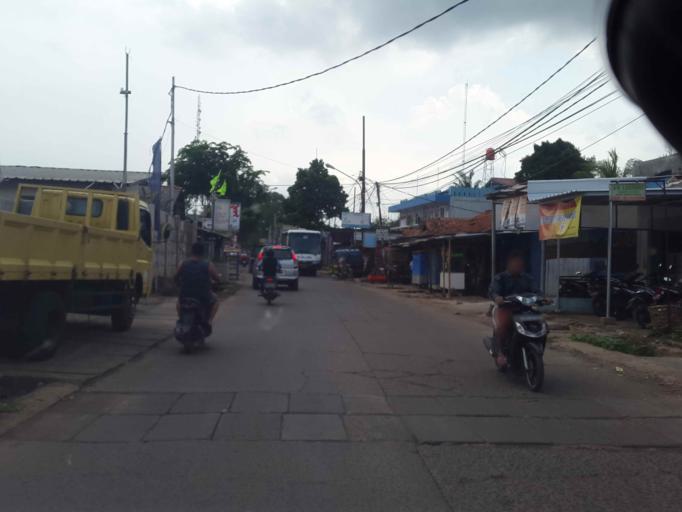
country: ID
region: West Java
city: Cileungsir
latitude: -6.3223
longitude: 106.9480
